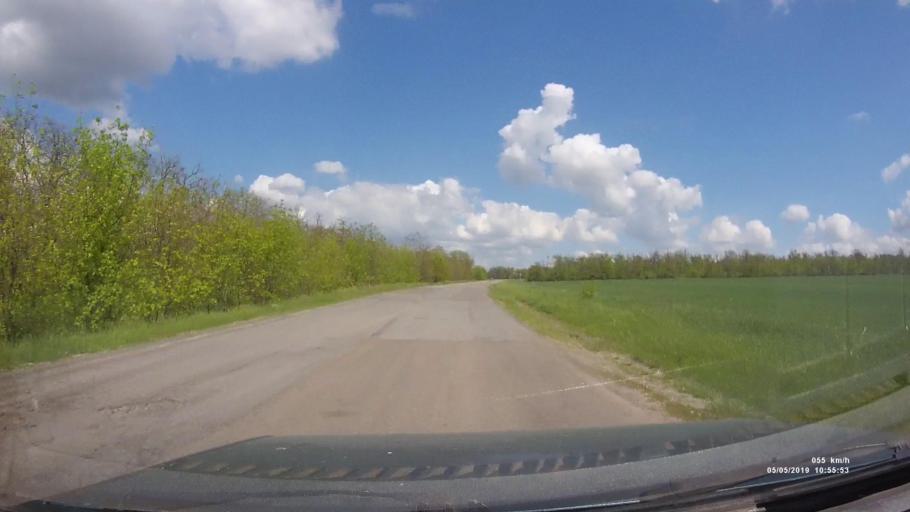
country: RU
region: Rostov
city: Ust'-Donetskiy
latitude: 47.6694
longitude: 40.8202
